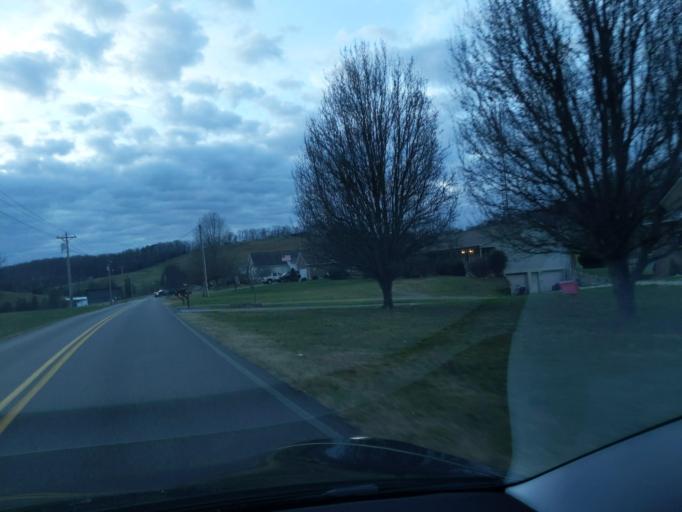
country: US
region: Tennessee
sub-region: Jefferson County
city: White Pine
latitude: 36.1074
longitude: -83.3571
